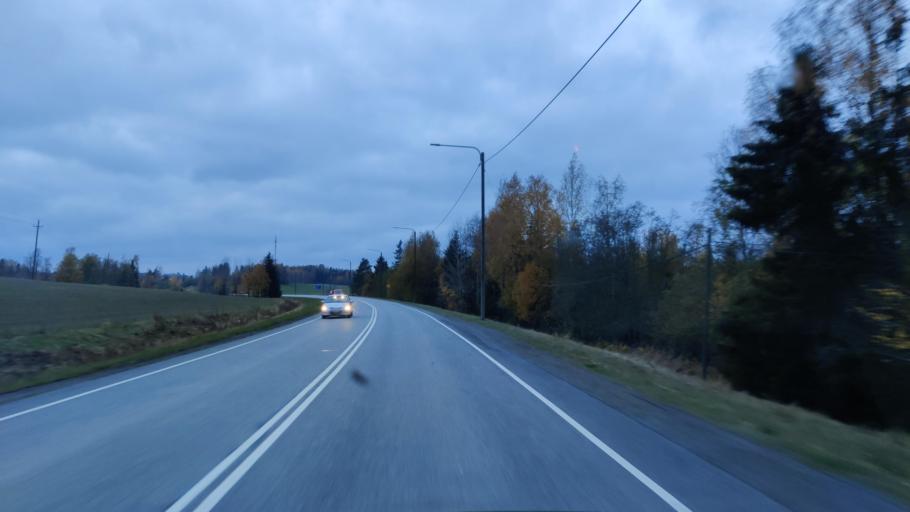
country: FI
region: Uusimaa
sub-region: Helsinki
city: Lohja
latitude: 60.3670
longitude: 24.1609
